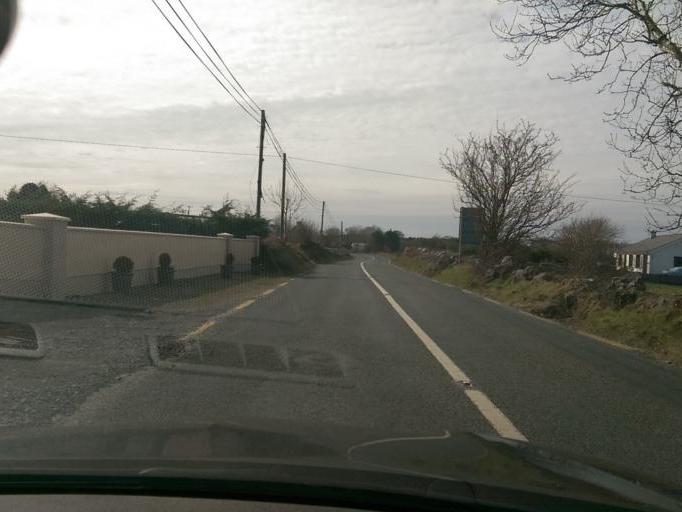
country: IE
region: Connaught
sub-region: County Galway
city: Tuam
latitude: 53.4238
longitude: -8.7830
